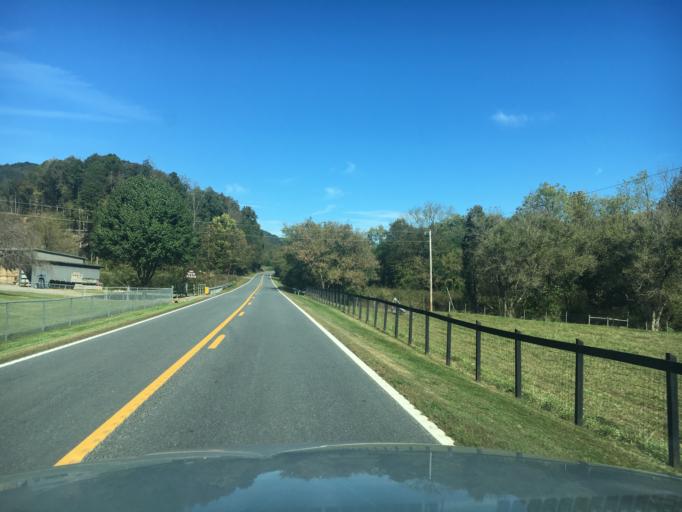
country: US
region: North Carolina
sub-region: Rutherford County
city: Spindale
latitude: 35.5256
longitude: -81.8554
